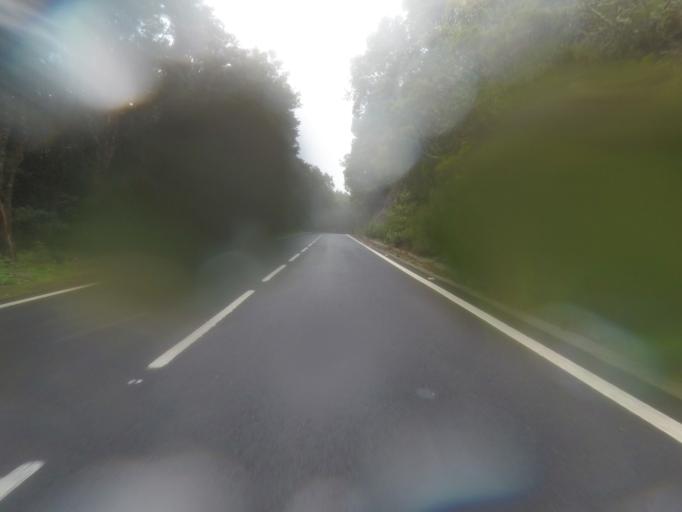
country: ES
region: Canary Islands
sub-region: Provincia de Santa Cruz de Tenerife
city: Vallehermosa
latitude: 28.1457
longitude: -17.2885
